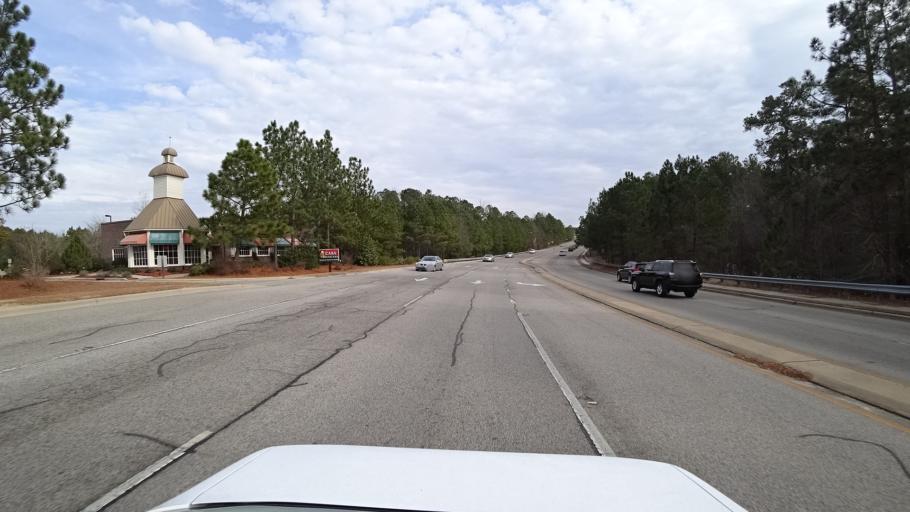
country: US
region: North Carolina
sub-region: Moore County
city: Southern Pines
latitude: 35.1781
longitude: -79.4274
